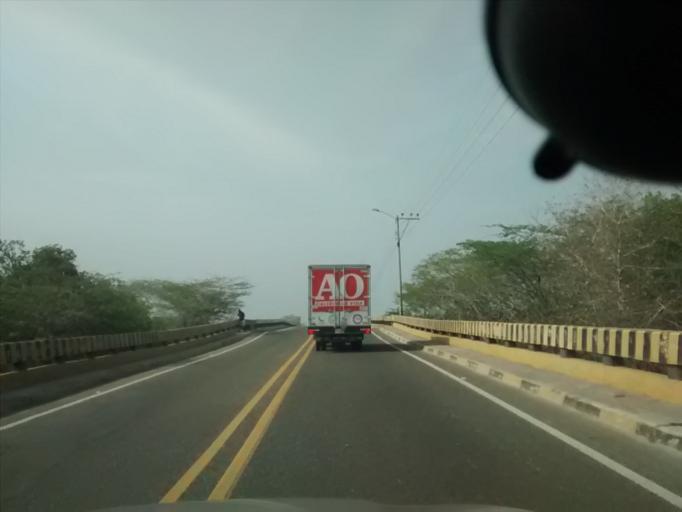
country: CO
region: Bolivar
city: Cartagena
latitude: 10.4837
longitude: -75.4867
